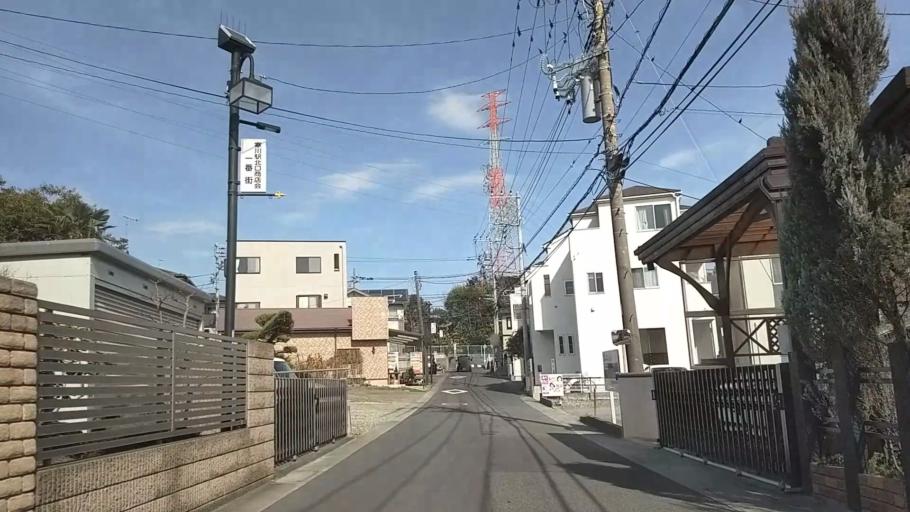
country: JP
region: Kanagawa
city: Chigasaki
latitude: 35.3719
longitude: 139.3894
